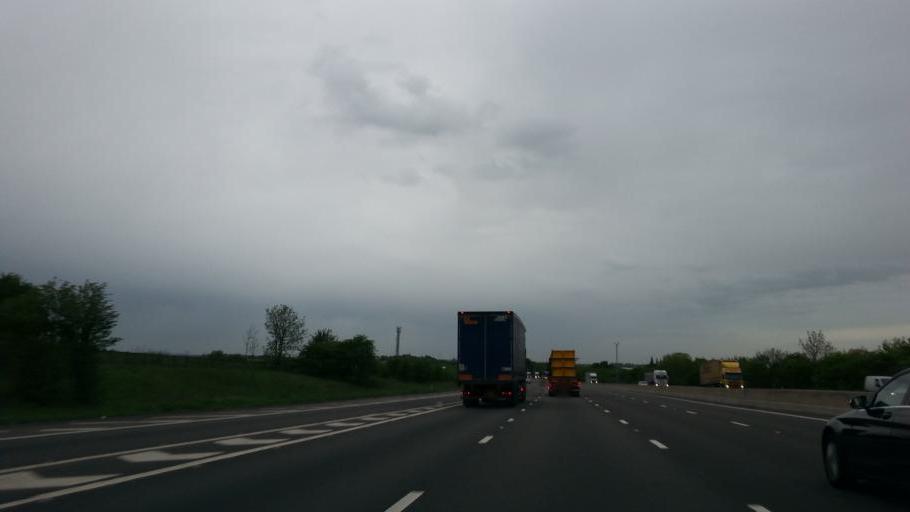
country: GB
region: England
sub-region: Rotherham
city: Harthill
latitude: 53.3178
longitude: -1.2815
